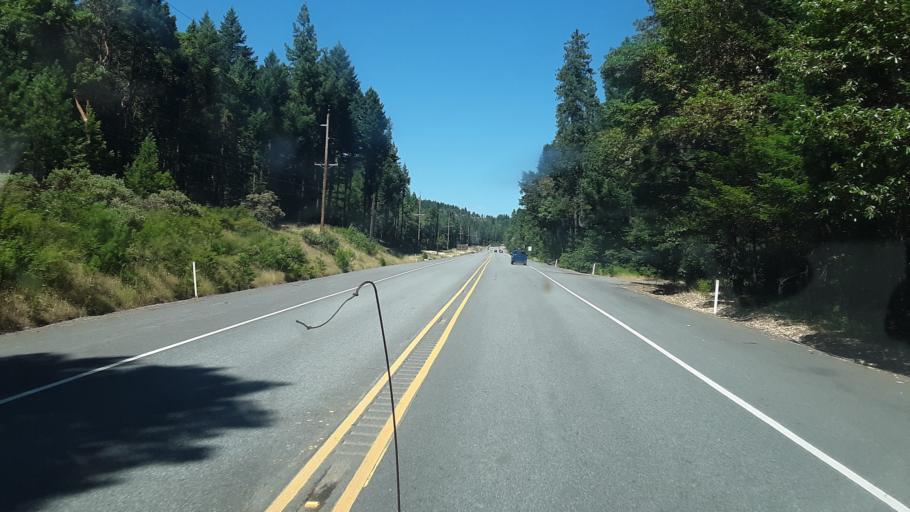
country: US
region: Oregon
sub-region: Josephine County
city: Cave Junction
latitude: 42.3218
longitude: -123.5978
